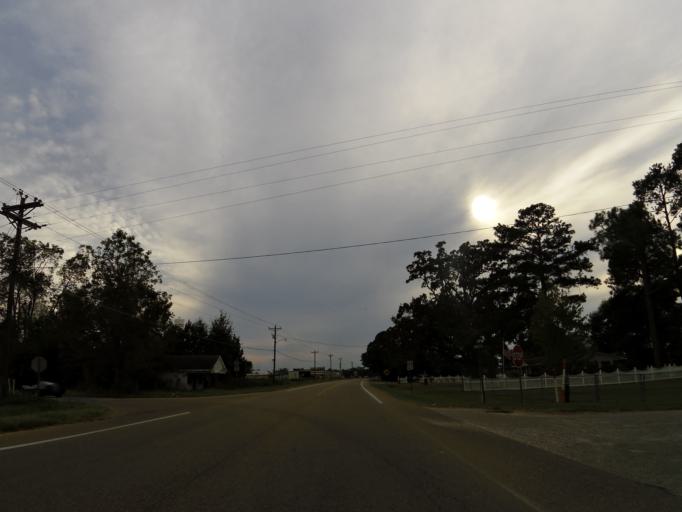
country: US
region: Alabama
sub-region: Monroe County
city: Frisco City
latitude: 31.4241
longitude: -87.4119
